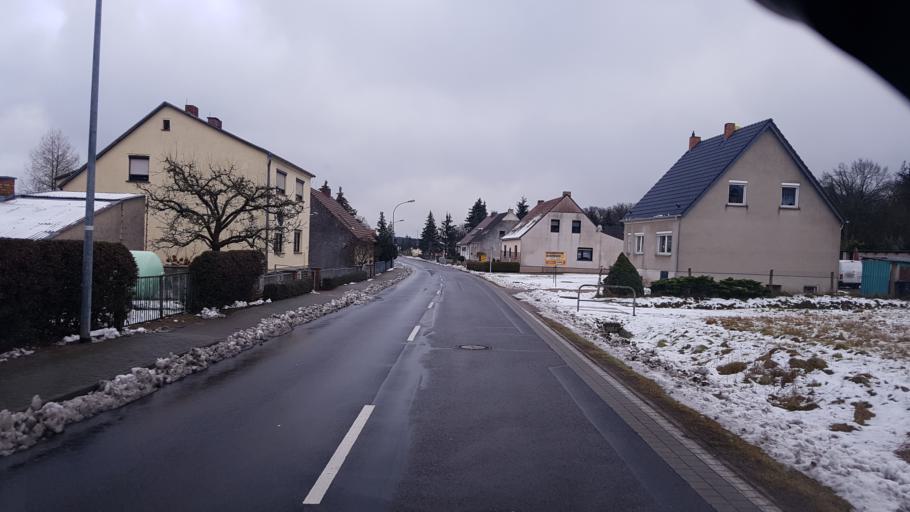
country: DE
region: Brandenburg
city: Schenkendobern
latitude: 51.9715
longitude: 14.5675
